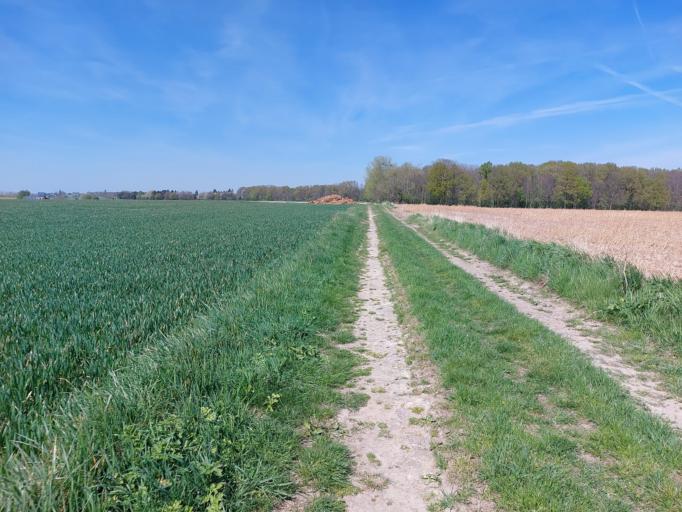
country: BE
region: Wallonia
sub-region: Province du Hainaut
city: Silly
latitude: 50.6124
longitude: 3.9704
